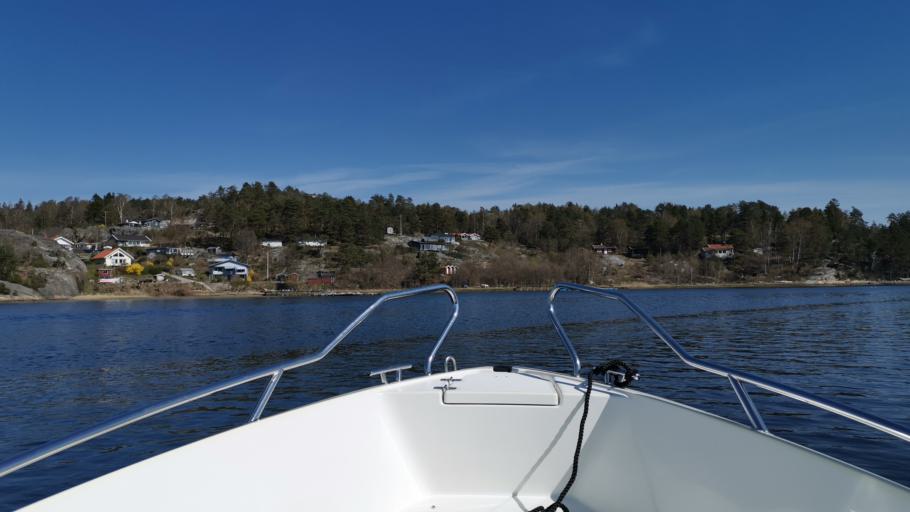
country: SE
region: Vaestra Goetaland
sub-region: Orust
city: Henan
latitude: 58.2574
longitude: 11.5783
